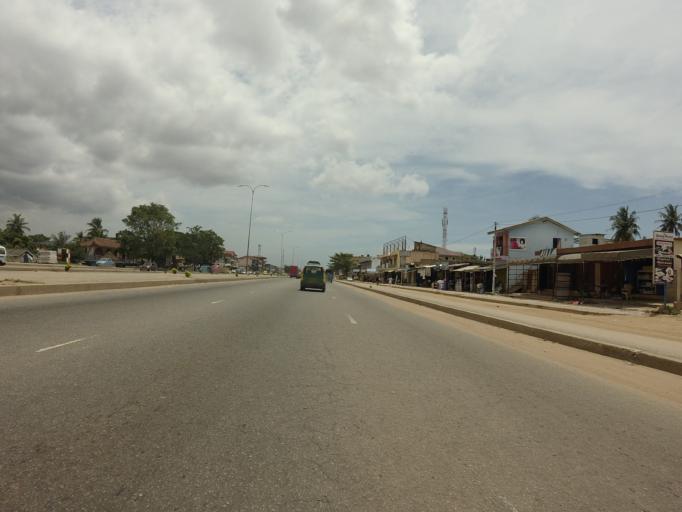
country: GH
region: Greater Accra
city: Gbawe
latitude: 5.5792
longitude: -0.2593
